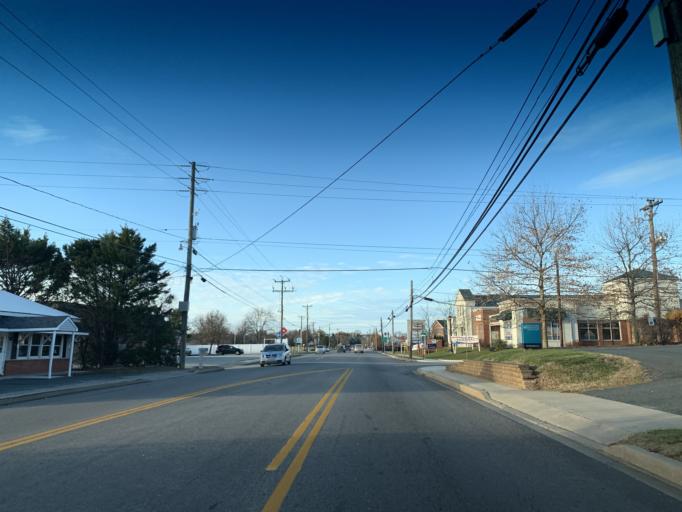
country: US
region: Maryland
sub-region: Kent County
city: Chestertown
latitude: 39.2218
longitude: -76.0687
